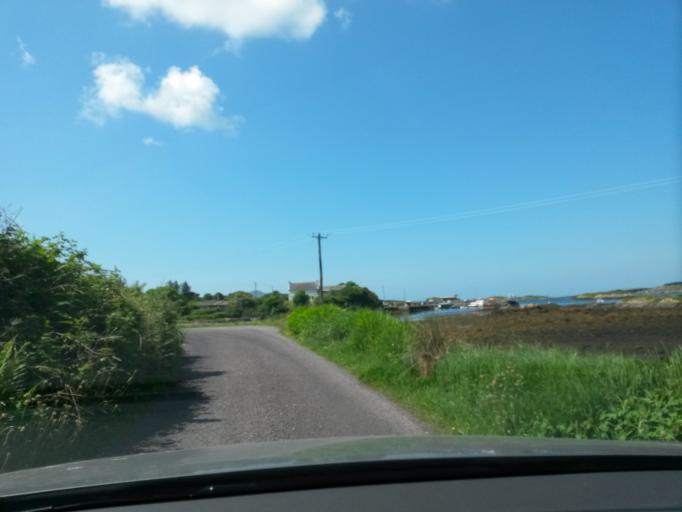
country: IE
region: Munster
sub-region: Ciarrai
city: Cahersiveen
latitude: 51.7147
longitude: -9.9451
